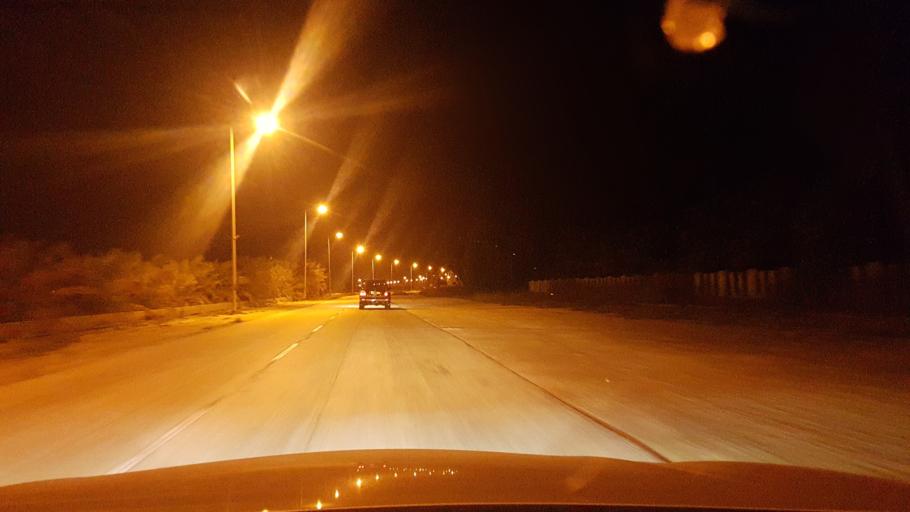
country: BH
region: Central Governorate
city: Dar Kulayb
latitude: 26.0293
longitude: 50.4824
